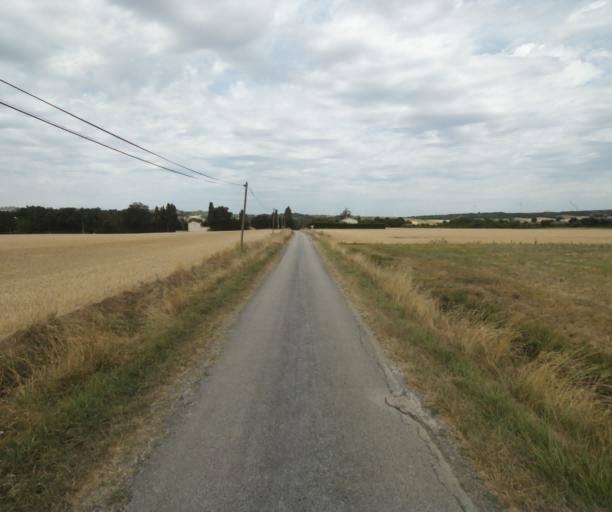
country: FR
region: Midi-Pyrenees
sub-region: Departement de la Haute-Garonne
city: Saint-Felix-Lauragais
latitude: 43.4403
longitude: 1.9299
